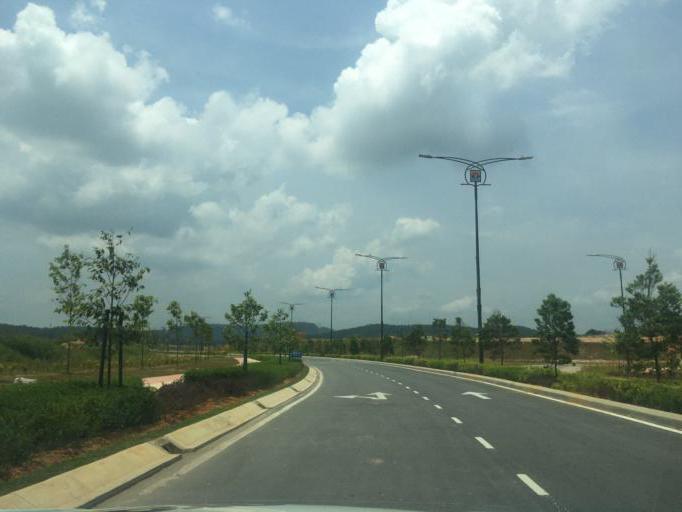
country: MY
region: Putrajaya
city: Putrajaya
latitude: 2.8454
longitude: 101.7001
